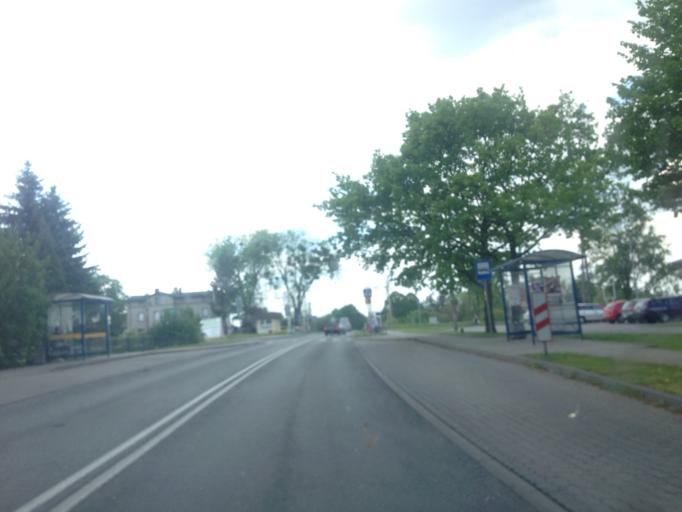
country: PL
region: Kujawsko-Pomorskie
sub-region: Powiat swiecki
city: Pruszcz
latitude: 53.2861
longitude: 18.1254
